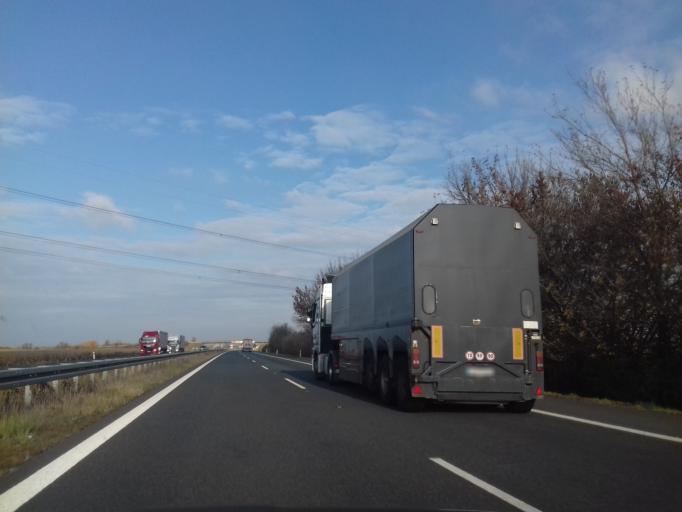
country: CZ
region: South Moravian
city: Kostice
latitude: 48.7609
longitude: 16.9473
